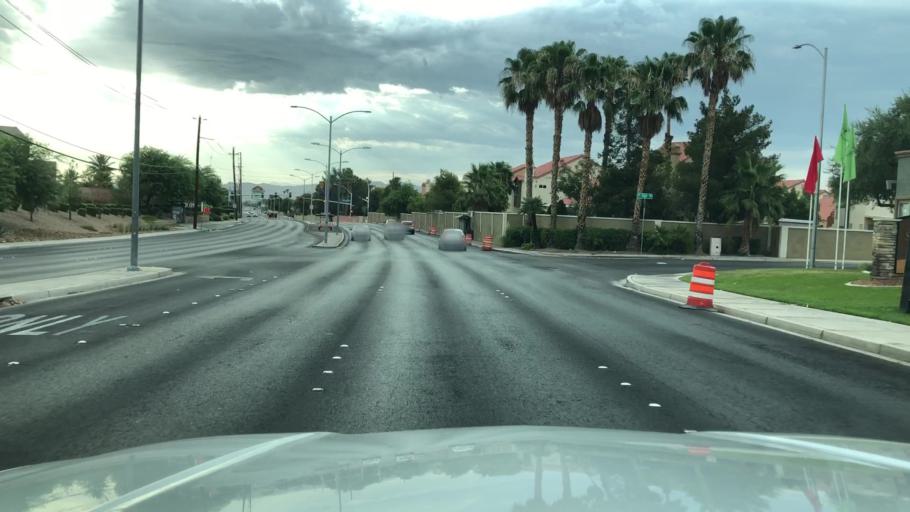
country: US
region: Nevada
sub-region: Clark County
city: Whitney
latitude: 36.0639
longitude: -115.0612
